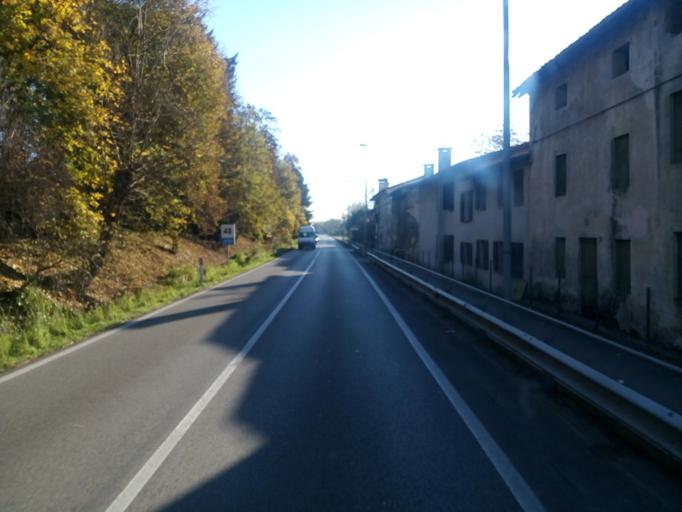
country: IT
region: Veneto
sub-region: Provincia di Vicenza
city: Cassola
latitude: 45.7175
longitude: 11.7847
